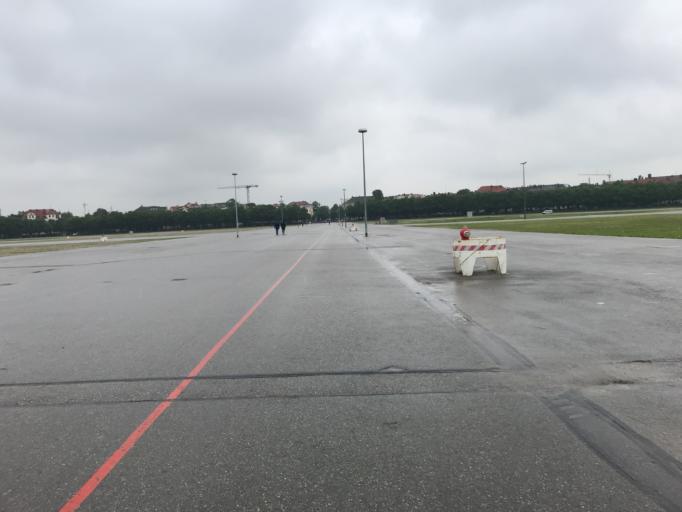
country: DE
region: Bavaria
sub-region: Upper Bavaria
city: Munich
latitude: 48.1305
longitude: 11.5472
